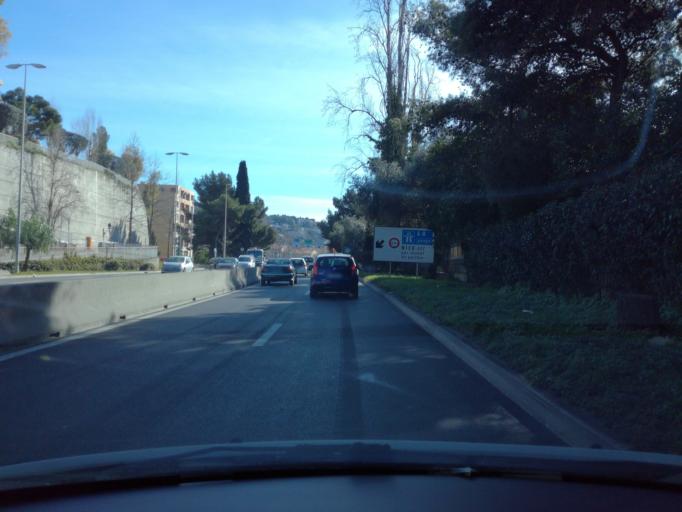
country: FR
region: Provence-Alpes-Cote d'Azur
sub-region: Departement des Alpes-Maritimes
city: Nice
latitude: 43.7070
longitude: 7.2780
